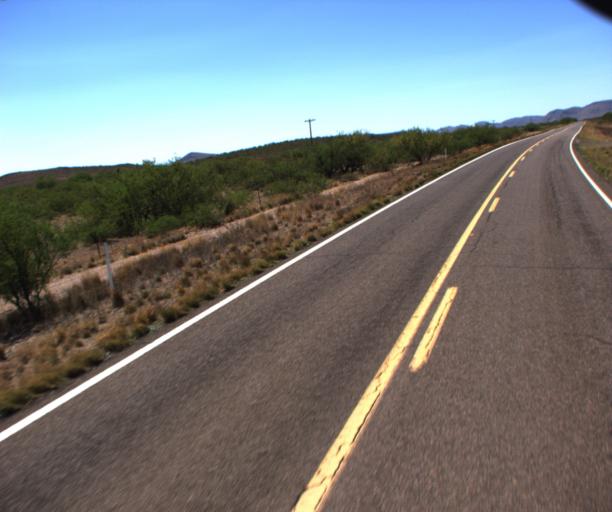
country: US
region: Arizona
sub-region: Cochise County
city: Douglas
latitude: 31.5132
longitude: -109.3099
